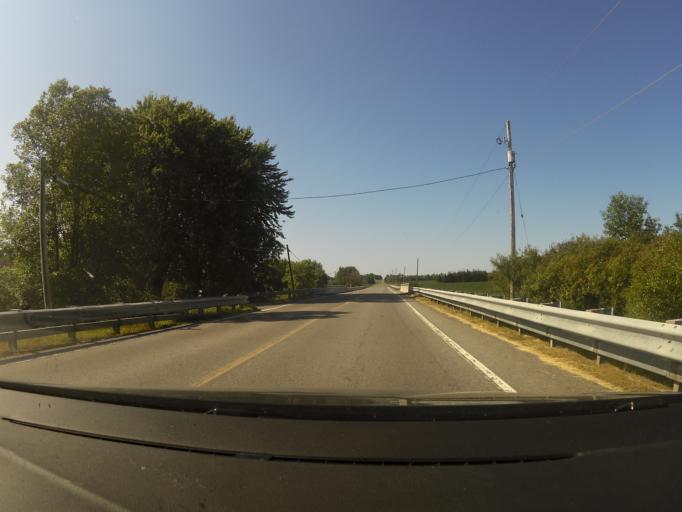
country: CA
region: Ontario
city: Carleton Place
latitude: 45.3670
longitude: -76.1099
